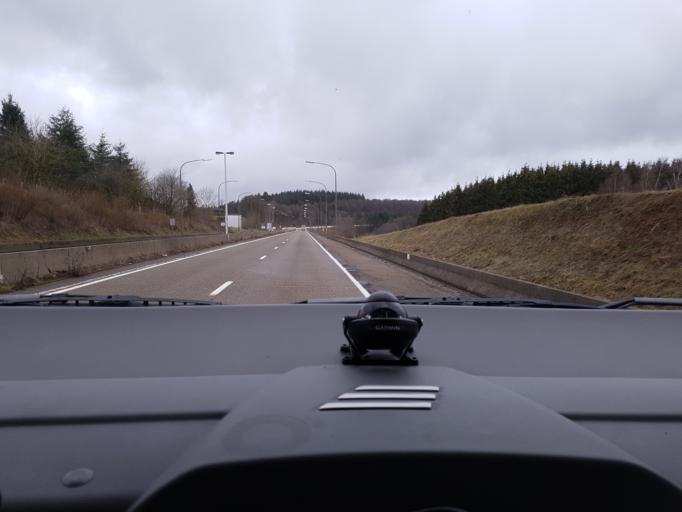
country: BE
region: Wallonia
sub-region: Province du Luxembourg
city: Tenneville
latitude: 50.0929
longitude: 5.4968
